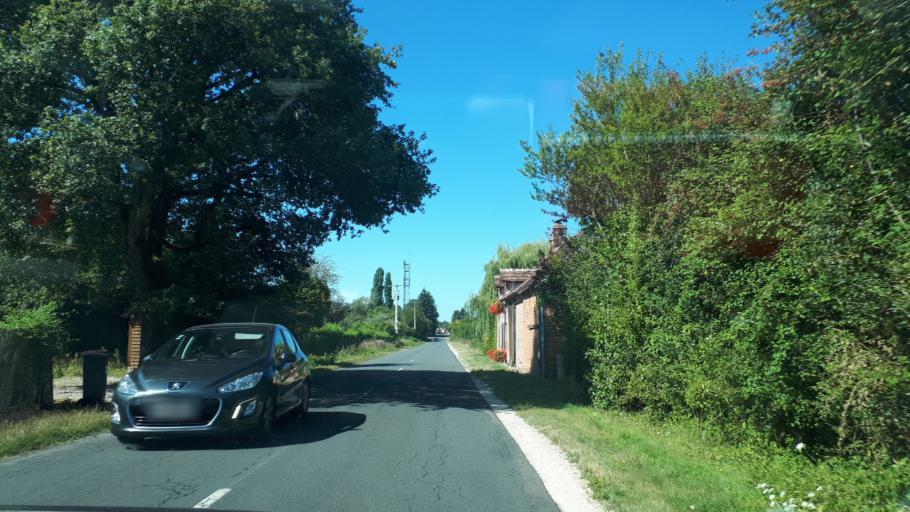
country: FR
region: Centre
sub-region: Departement du Cher
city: Brinon-sur-Sauldre
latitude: 47.6474
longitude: 2.1751
